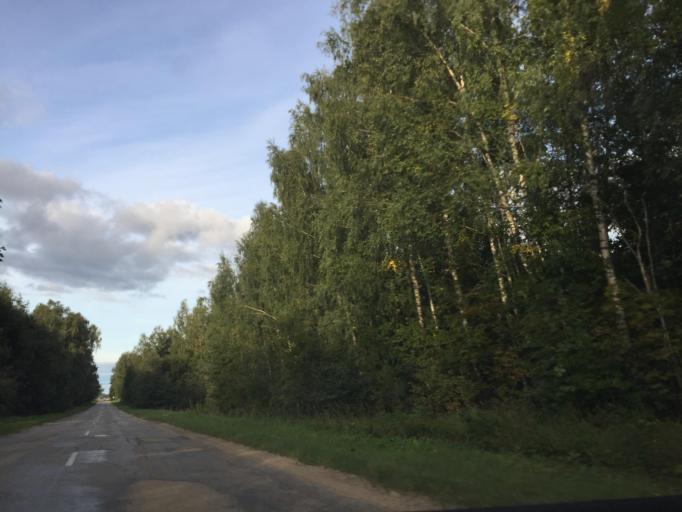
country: LV
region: Nereta
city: Nereta
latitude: 56.2580
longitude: 25.3493
